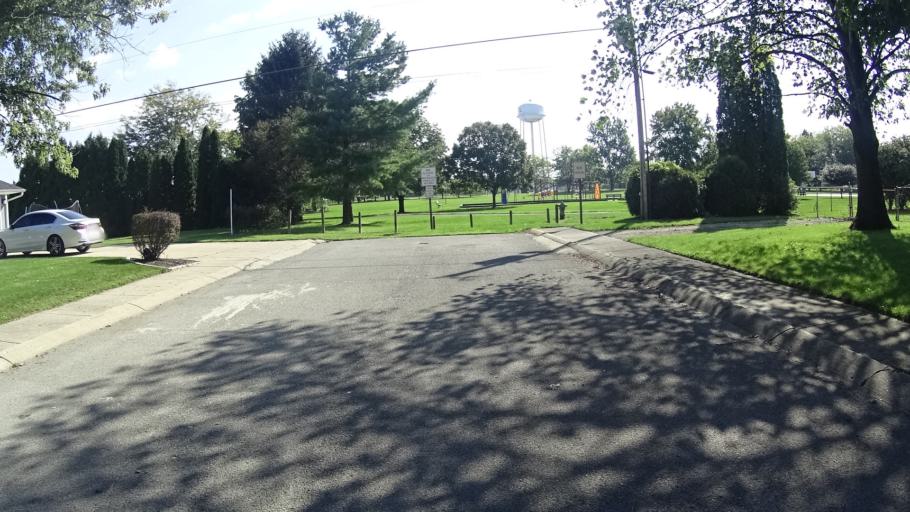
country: US
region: Indiana
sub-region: Madison County
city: Lapel
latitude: 40.0743
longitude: -85.8466
